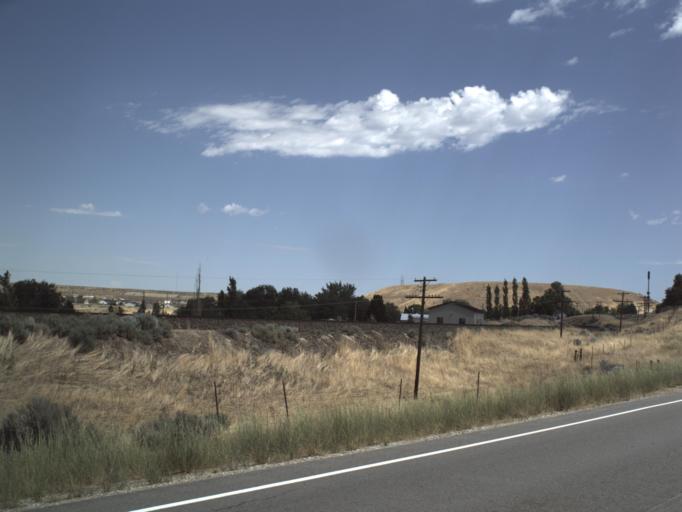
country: US
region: Utah
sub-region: Tooele County
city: Tooele
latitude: 40.4438
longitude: -112.3669
